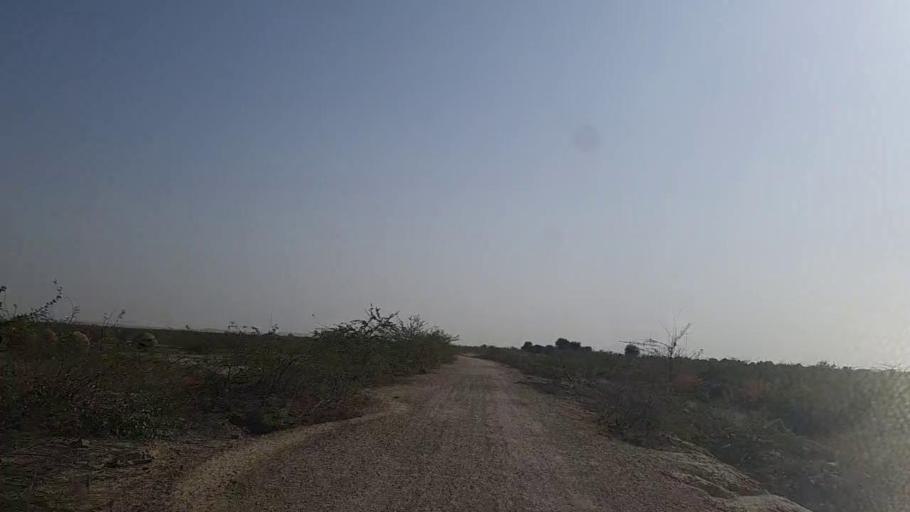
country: PK
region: Sindh
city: Naukot
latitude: 24.5941
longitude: 69.2629
